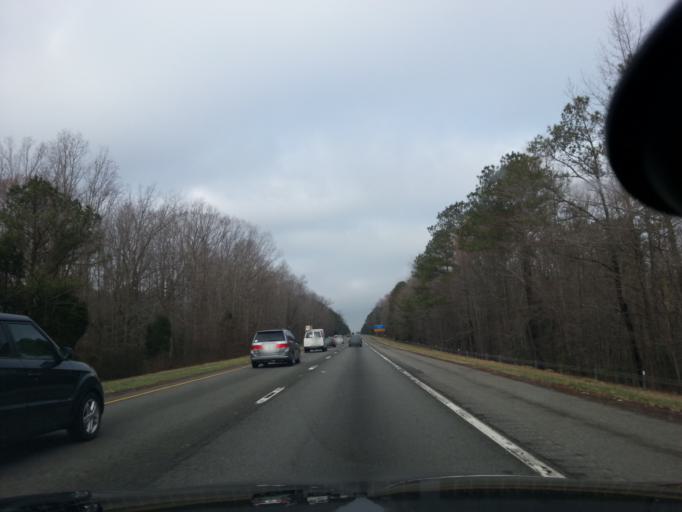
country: US
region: Virginia
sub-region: New Kent County
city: New Kent
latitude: 37.5088
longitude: -77.1156
